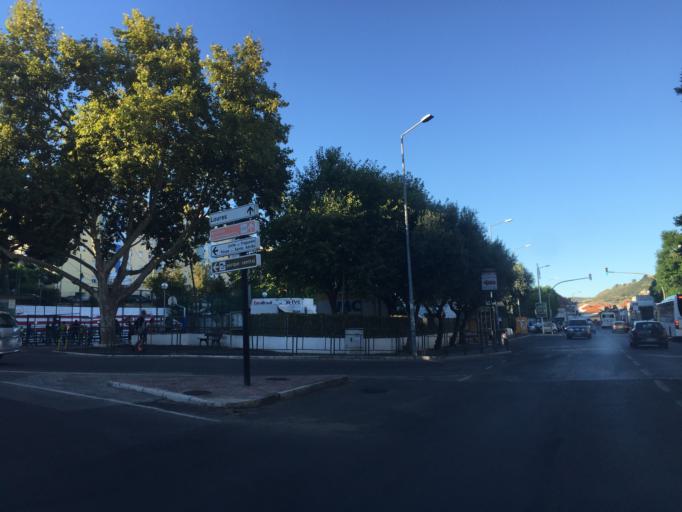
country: PT
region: Lisbon
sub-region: Odivelas
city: Povoa de Santo Adriao
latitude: 38.7975
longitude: -9.1620
